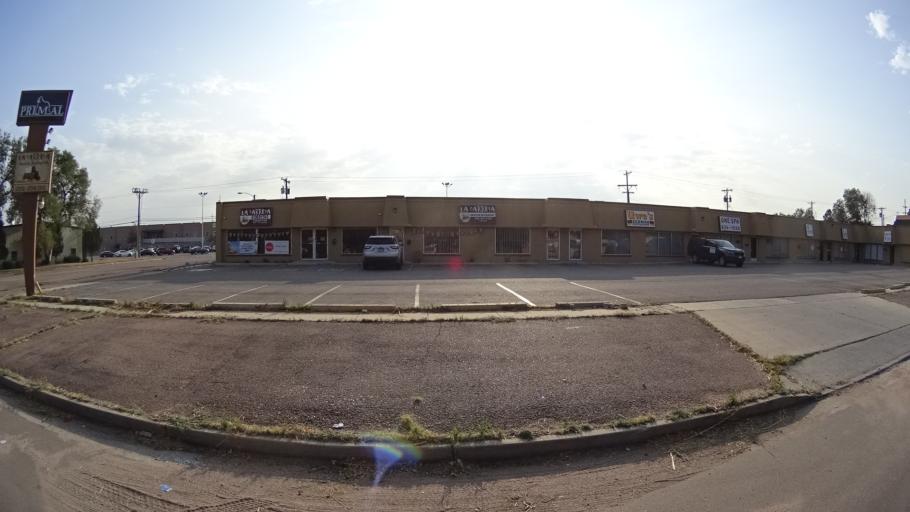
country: US
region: Colorado
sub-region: El Paso County
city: Colorado Springs
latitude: 38.8342
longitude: -104.7900
